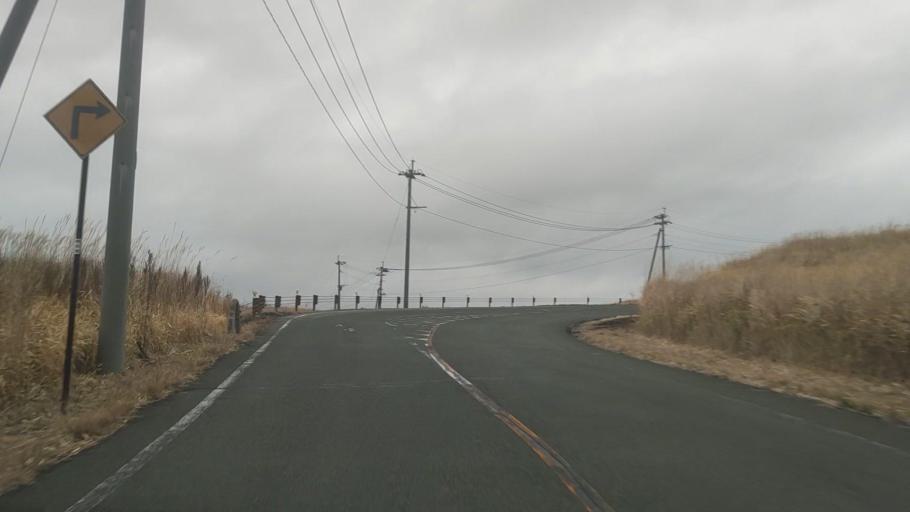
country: JP
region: Kumamoto
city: Aso
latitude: 32.9029
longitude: 131.0351
